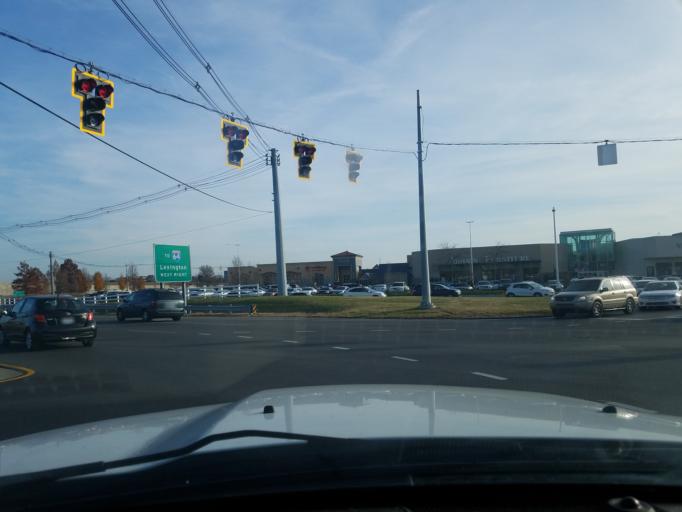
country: US
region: Kentucky
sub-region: Jefferson County
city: Beechwood Village
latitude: 38.2502
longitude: -85.6235
